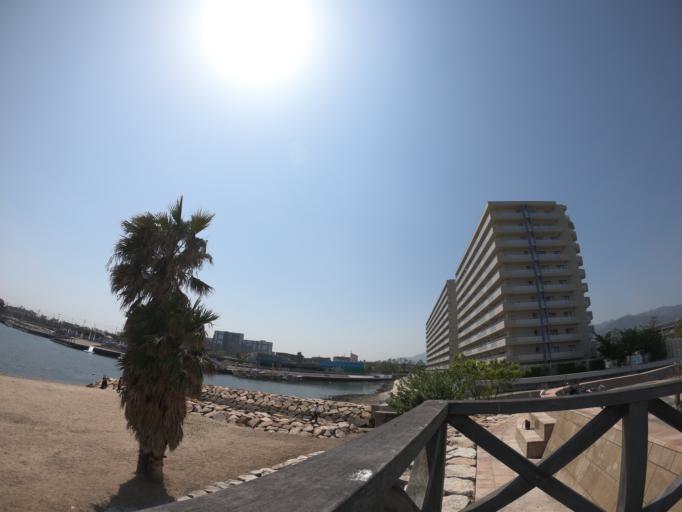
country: JP
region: Hyogo
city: Nishinomiya-hama
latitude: 34.7259
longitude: 135.3247
